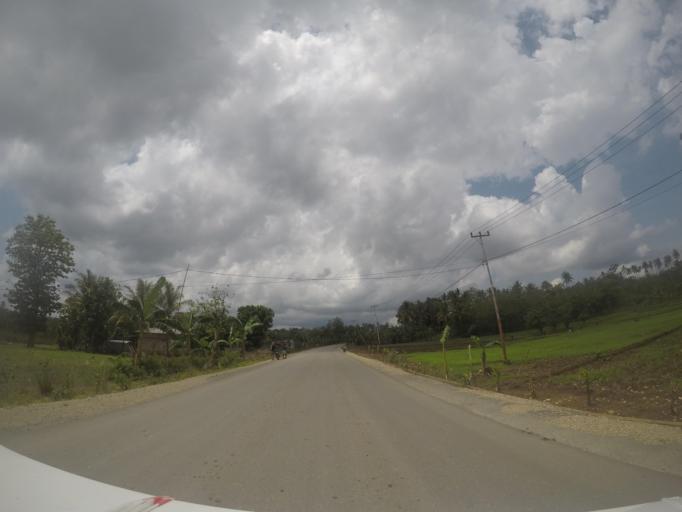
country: TL
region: Baucau
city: Baucau
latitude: -8.5380
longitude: 126.4187
